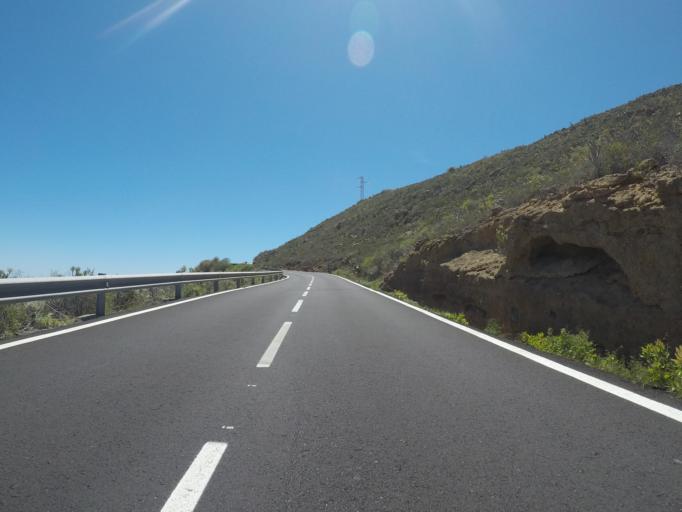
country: ES
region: Canary Islands
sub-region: Provincia de Santa Cruz de Tenerife
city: Lomo de Arico
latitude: 28.1689
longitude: -16.5010
